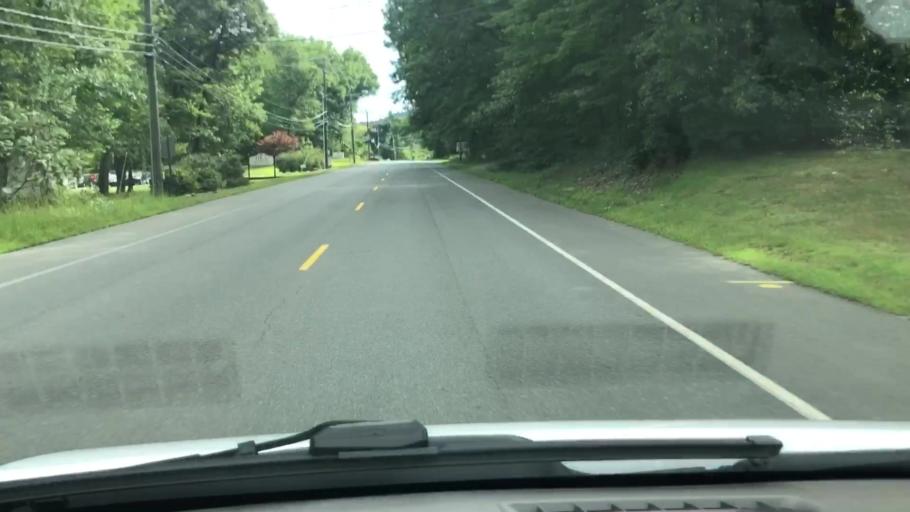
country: US
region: Massachusetts
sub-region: Franklin County
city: Turners Falls
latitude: 42.5893
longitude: -72.5305
